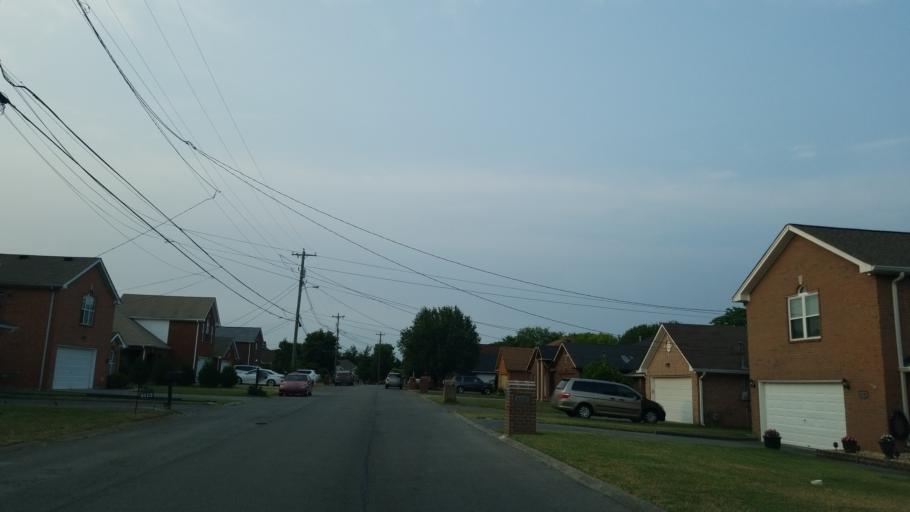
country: US
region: Tennessee
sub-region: Rutherford County
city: La Vergne
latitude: 36.0313
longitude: -86.5838
